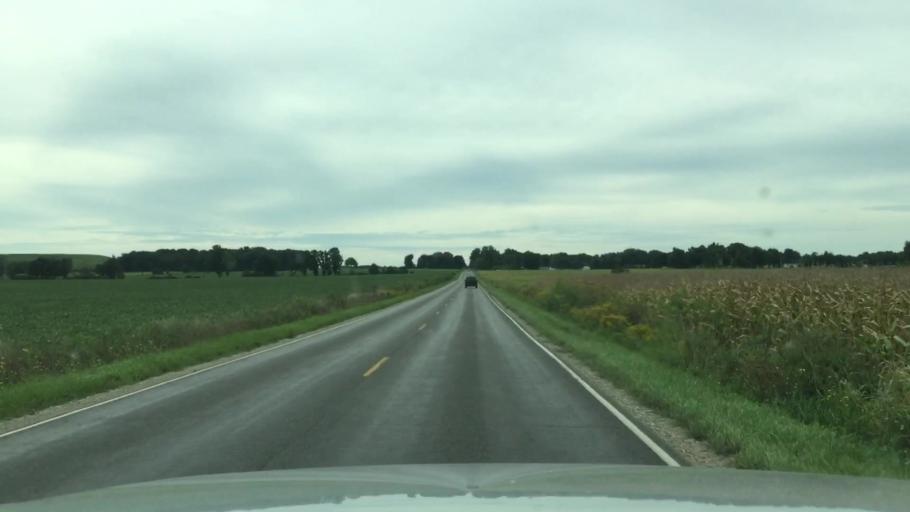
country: US
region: Michigan
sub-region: Shiawassee County
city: Durand
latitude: 42.9934
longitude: -83.9868
